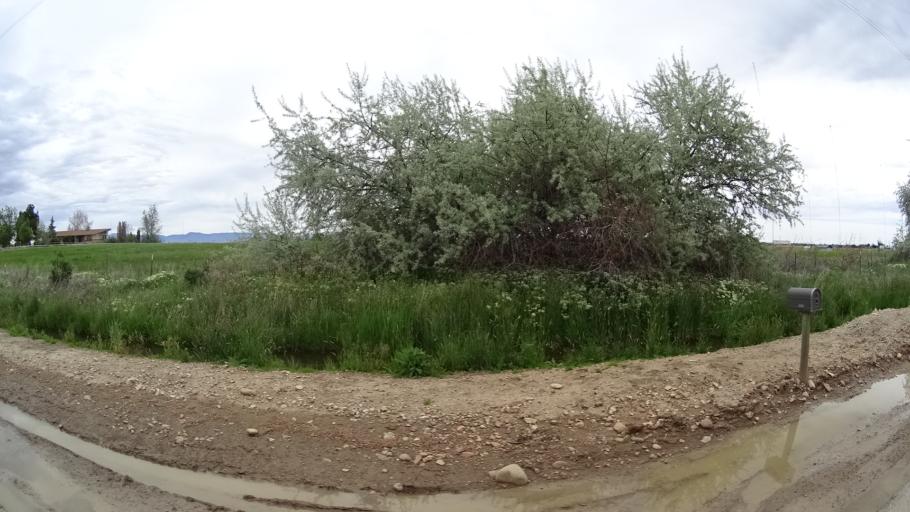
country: US
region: Idaho
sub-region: Ada County
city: Kuna
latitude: 43.5506
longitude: -116.4138
